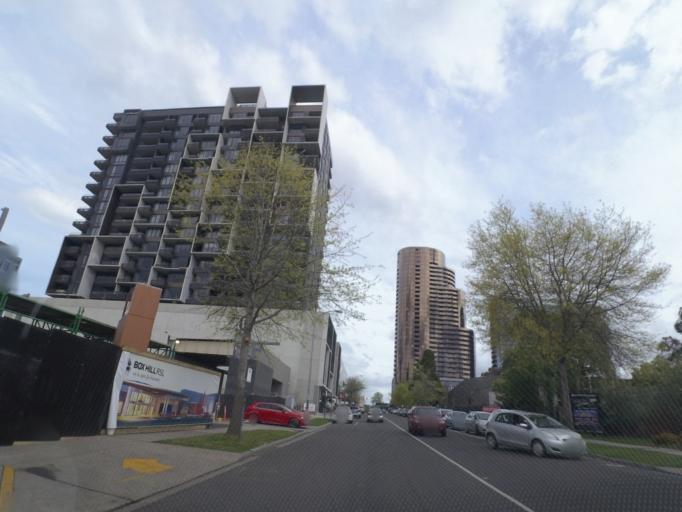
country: AU
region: Victoria
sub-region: Whitehorse
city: Box Hill
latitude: -37.8156
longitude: 145.1197
